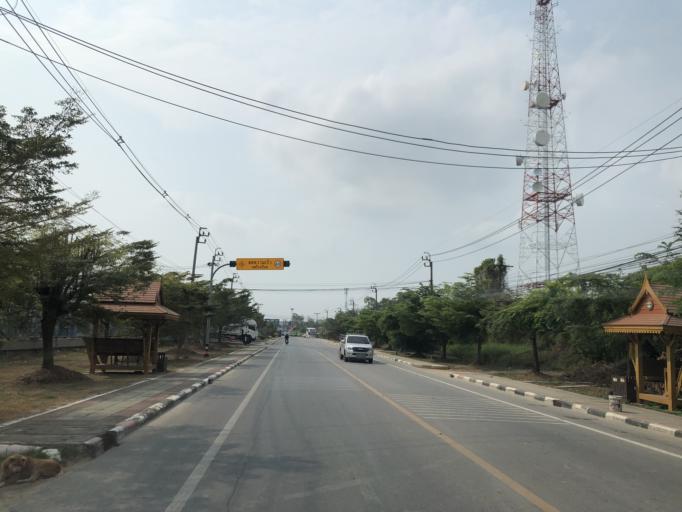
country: TH
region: Samut Prakan
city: Bang Bo District
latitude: 13.5843
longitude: 100.7425
